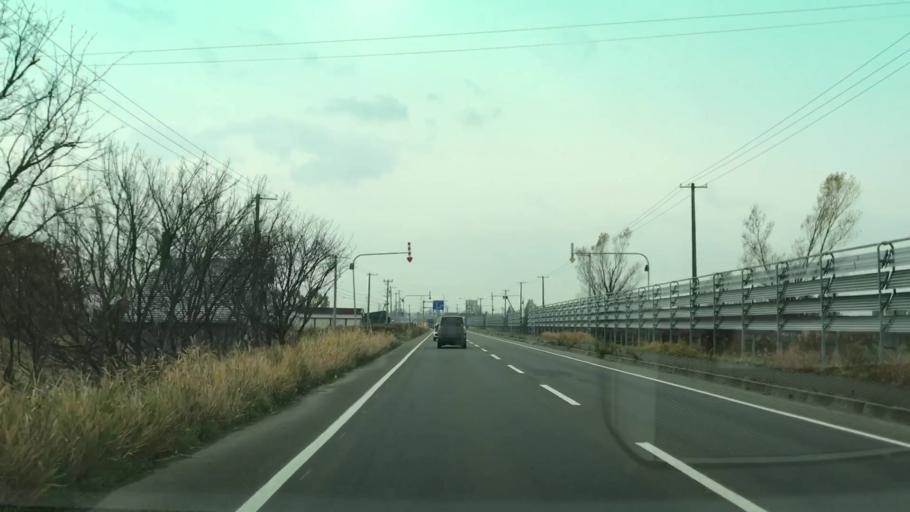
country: JP
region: Hokkaido
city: Ishikari
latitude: 43.2197
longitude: 141.3409
